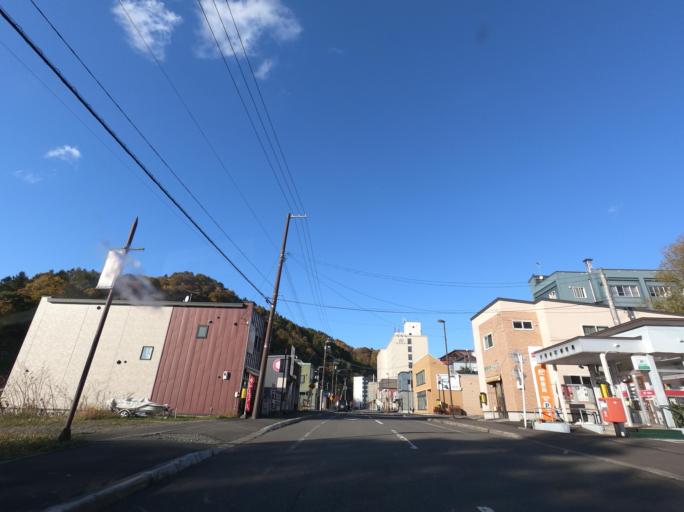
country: JP
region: Hokkaido
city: Iwamizawa
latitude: 43.0579
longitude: 141.9766
